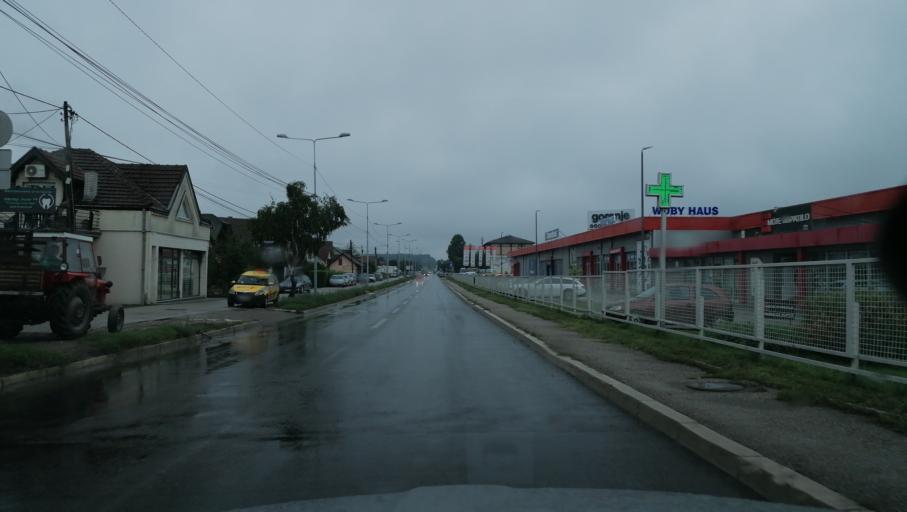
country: RS
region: Central Serbia
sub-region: Raski Okrug
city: Kraljevo
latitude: 43.7301
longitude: 20.6646
